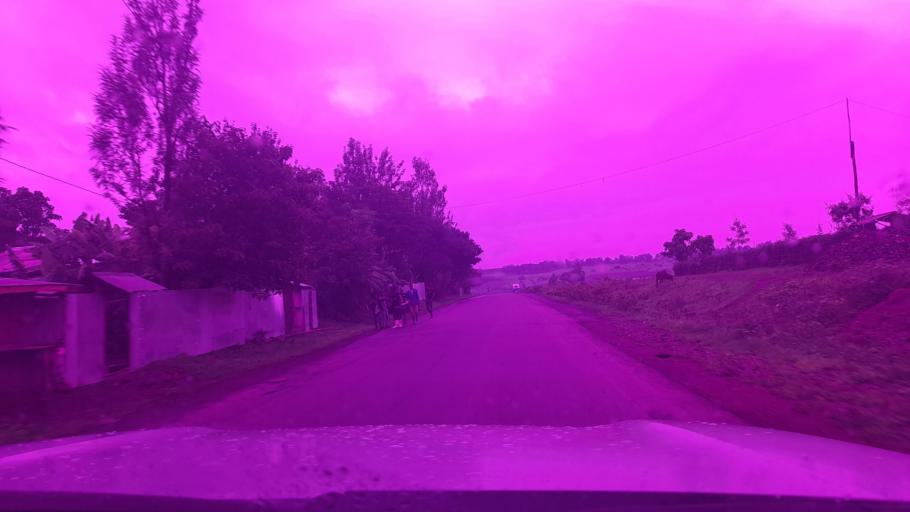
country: ET
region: Oromiya
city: Jima
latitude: 7.8317
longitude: 37.3486
